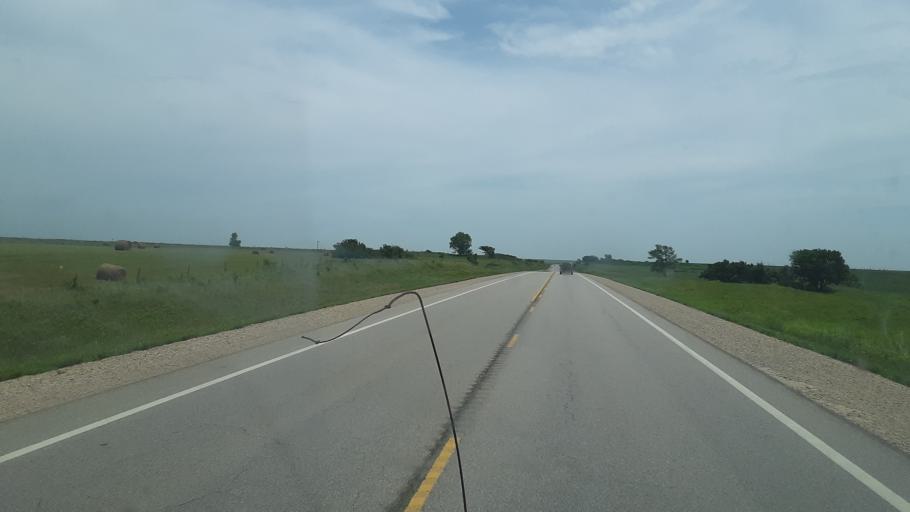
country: US
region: Kansas
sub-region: Greenwood County
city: Eureka
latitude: 37.8129
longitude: -96.4904
